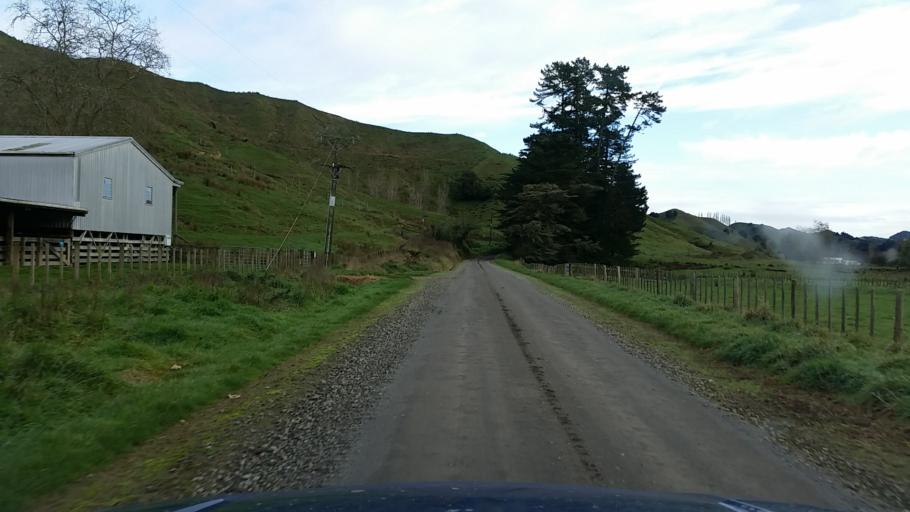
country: NZ
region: Taranaki
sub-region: New Plymouth District
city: Waitara
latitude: -39.0892
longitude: 174.8346
